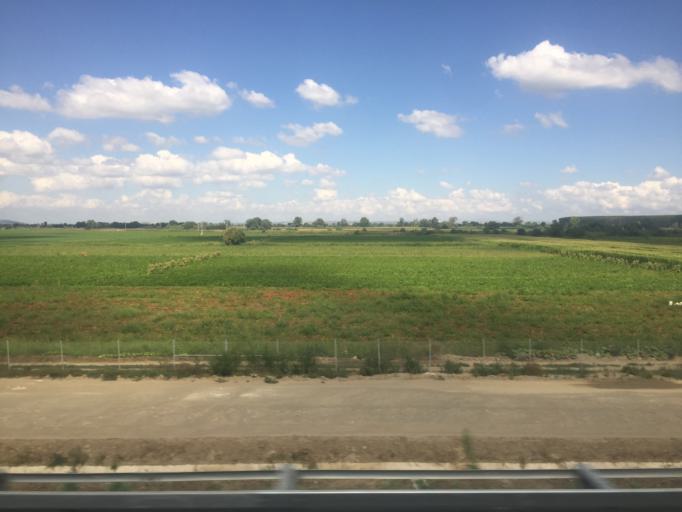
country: TR
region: Bursa
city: Tatkavakli
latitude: 40.0816
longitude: 28.2602
